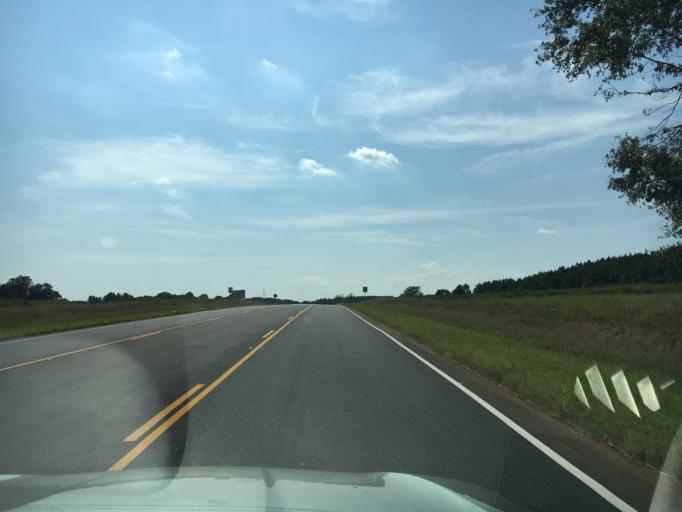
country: US
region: South Carolina
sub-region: Spartanburg County
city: Roebuck
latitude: 34.8724
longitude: -82.0280
